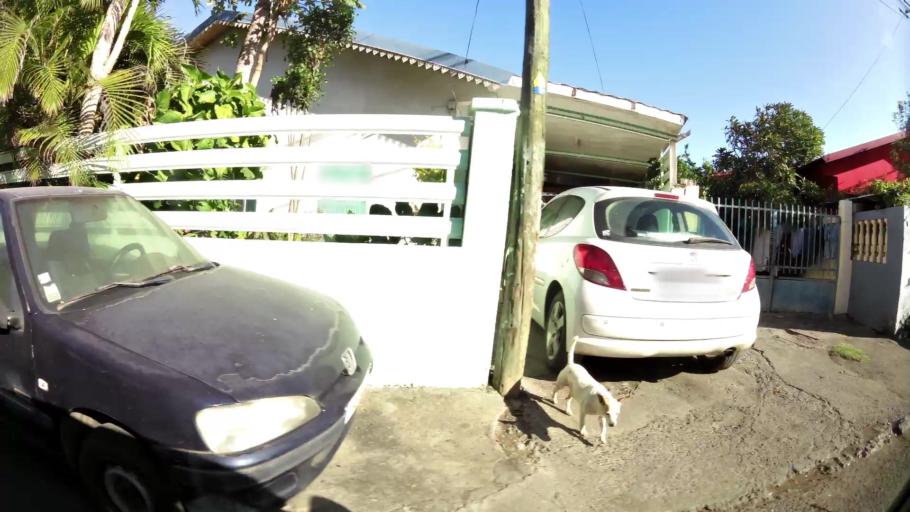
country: RE
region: Reunion
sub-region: Reunion
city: Saint-Louis
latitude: -21.2931
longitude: 55.3948
